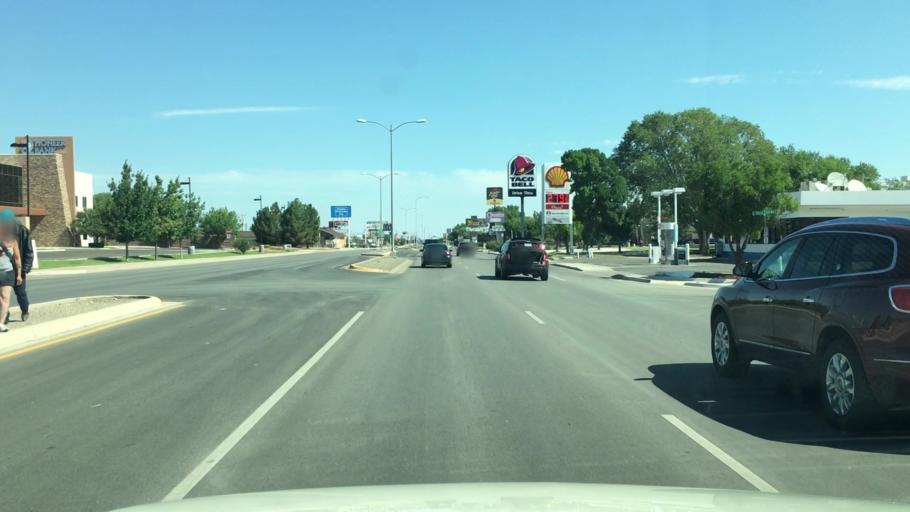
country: US
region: New Mexico
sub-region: Chaves County
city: Roswell
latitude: 33.4320
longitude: -104.5231
